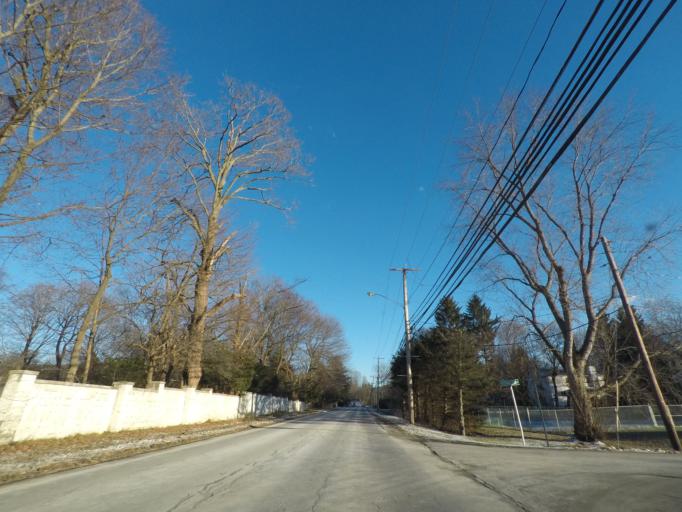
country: US
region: New York
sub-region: Rensselaer County
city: Poestenkill
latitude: 42.6951
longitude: -73.5752
